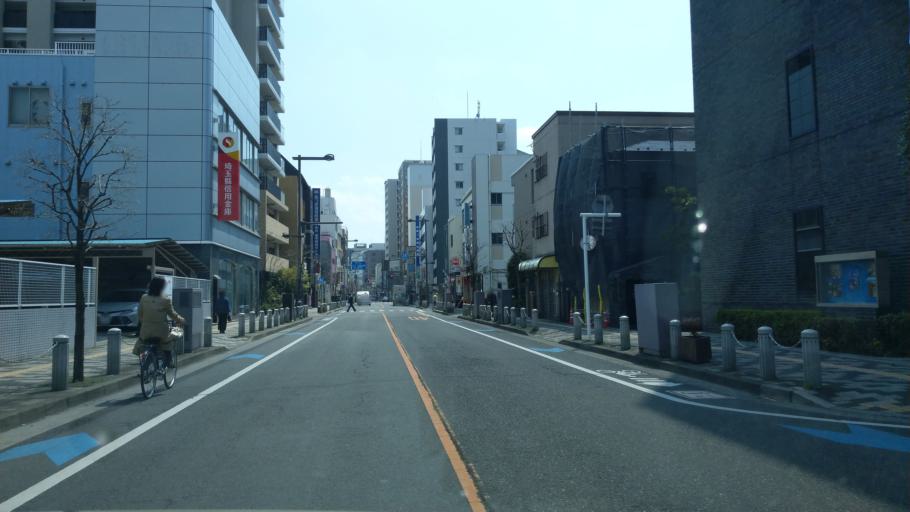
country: JP
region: Saitama
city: Yono
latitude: 35.8740
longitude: 139.6465
